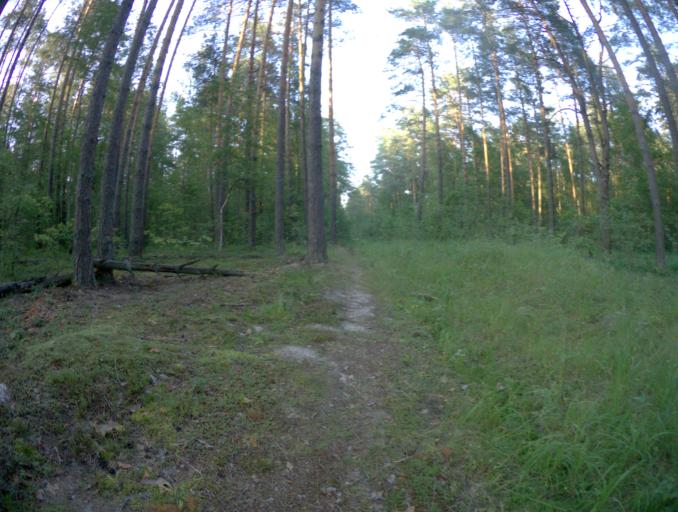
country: RU
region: Vladimir
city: Kommunar
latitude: 56.0935
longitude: 40.4530
